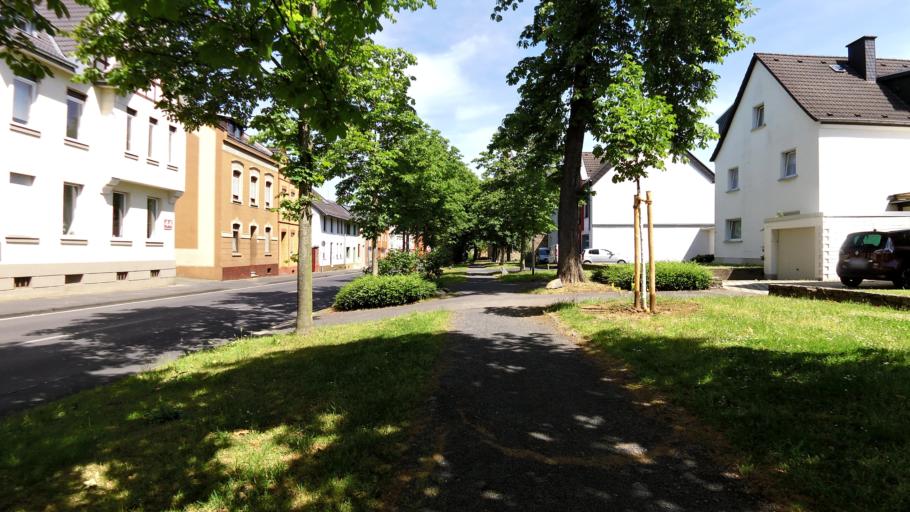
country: DE
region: North Rhine-Westphalia
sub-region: Regierungsbezirk Koln
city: Rheinbach
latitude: 50.6239
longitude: 6.9464
